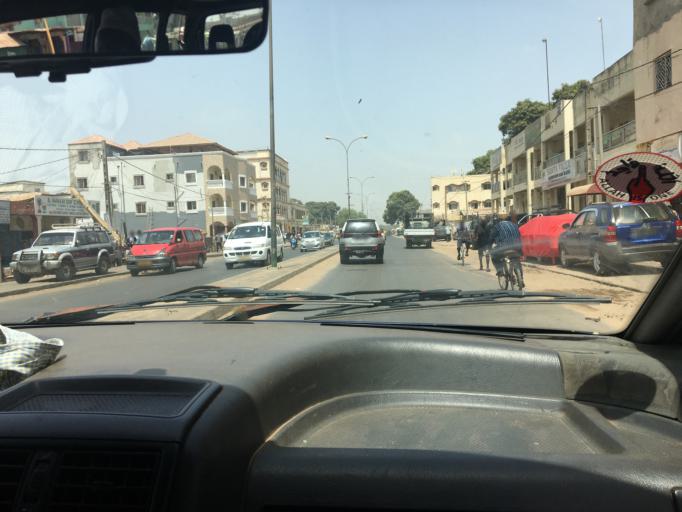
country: GM
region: Western
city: Abuko
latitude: 13.4074
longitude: -16.6664
